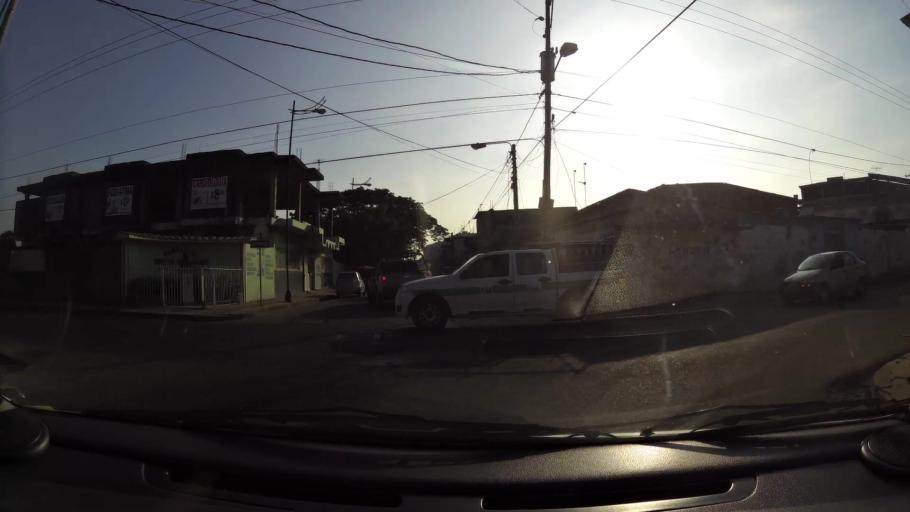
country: EC
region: Guayas
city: Eloy Alfaro
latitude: -2.1795
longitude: -79.8565
